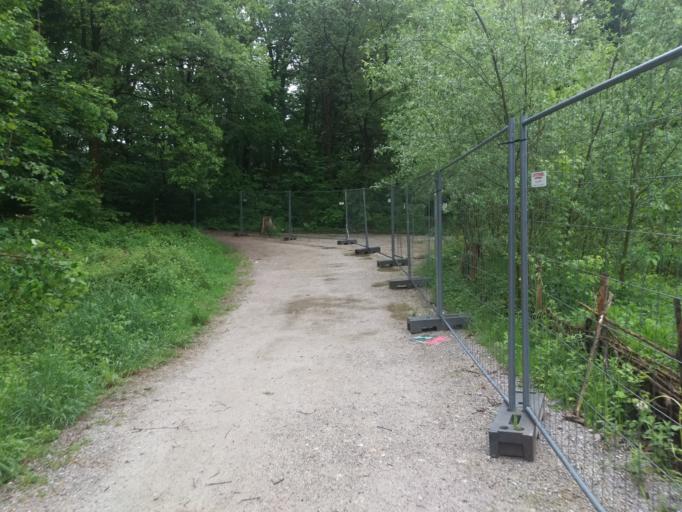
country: AT
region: Salzburg
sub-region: Politischer Bezirk Salzburg-Umgebung
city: Anif
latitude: 47.7532
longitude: 13.0721
